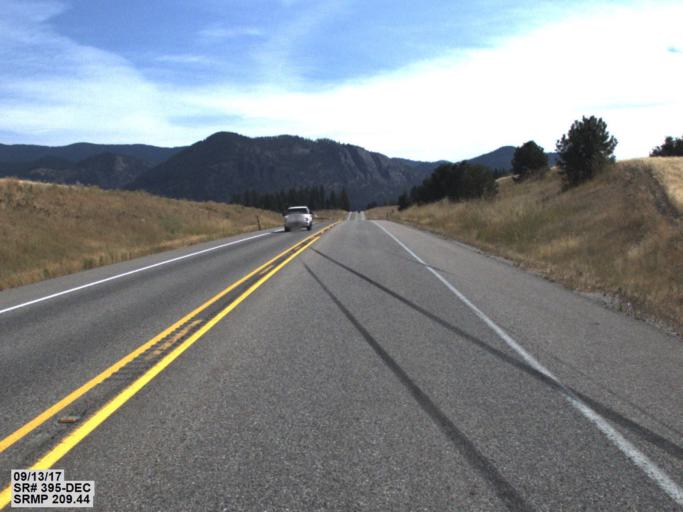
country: US
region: Washington
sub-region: Stevens County
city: Chewelah
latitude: 48.2962
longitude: -117.7497
